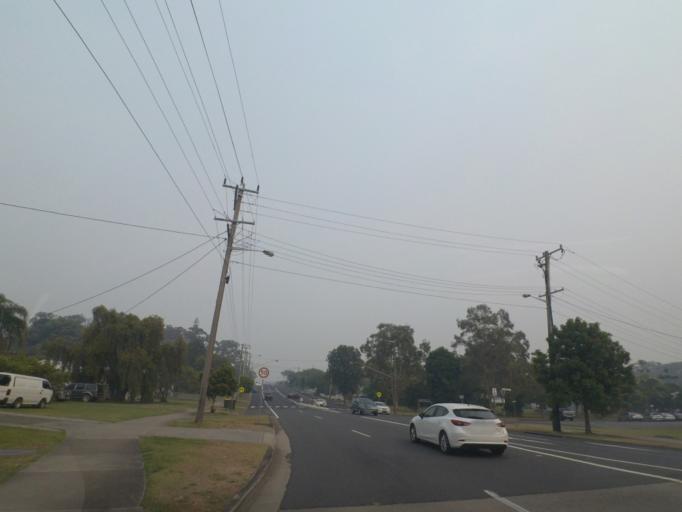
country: AU
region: New South Wales
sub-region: Coffs Harbour
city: Coffs Harbour
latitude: -30.3030
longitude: 153.1234
